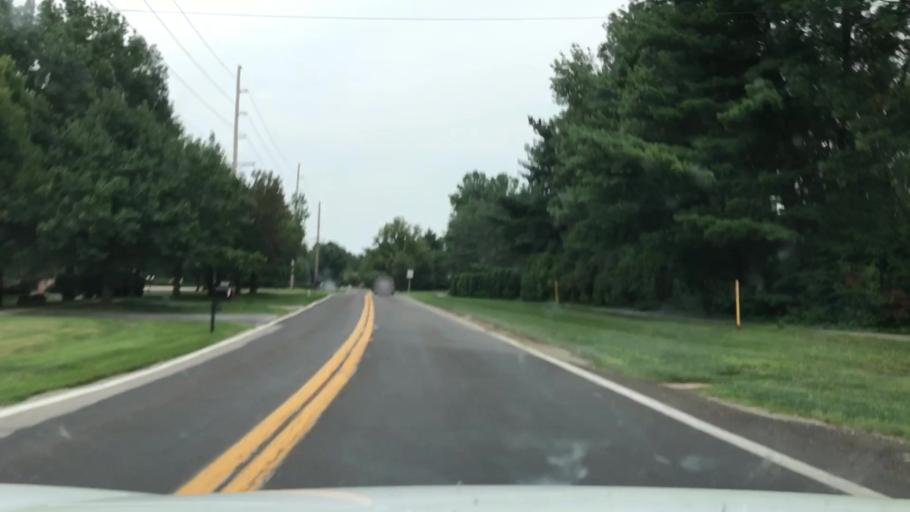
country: US
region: Missouri
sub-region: Saint Louis County
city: Clarkson Valley
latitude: 38.6281
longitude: -90.5965
